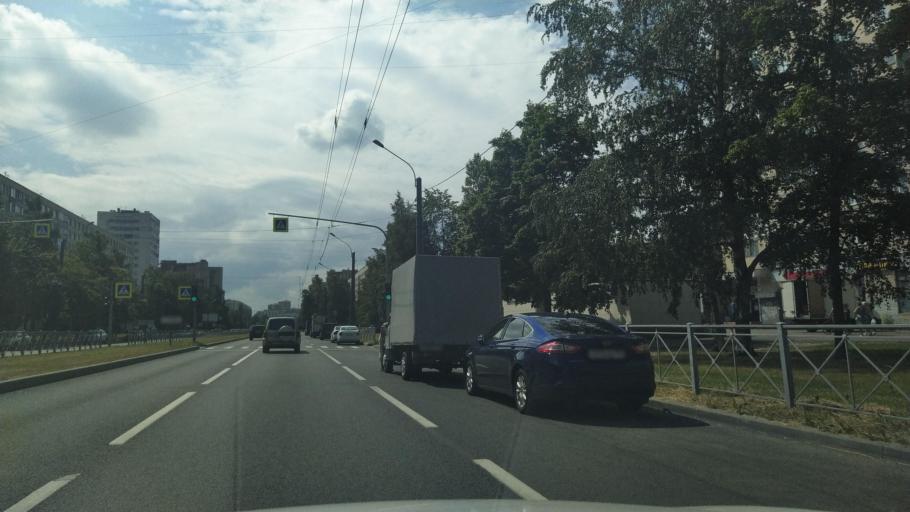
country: RU
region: Leningrad
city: Parnas
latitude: 60.0455
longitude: 30.3512
